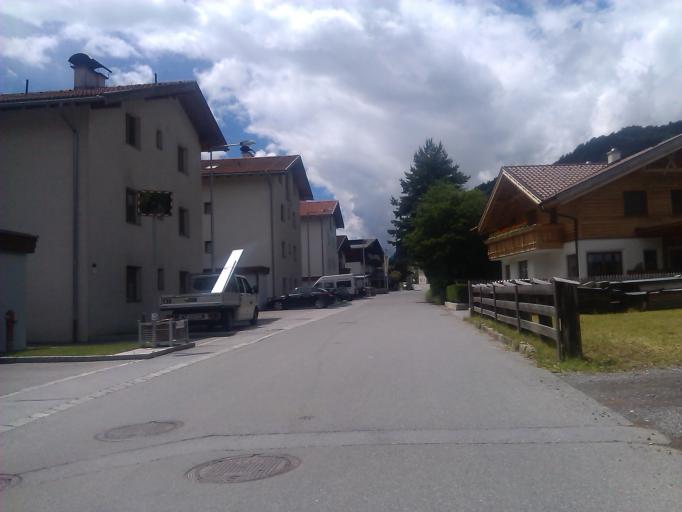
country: AT
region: Tyrol
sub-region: Politischer Bezirk Landeck
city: Ried im Oberinntal
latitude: 47.0513
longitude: 10.6497
